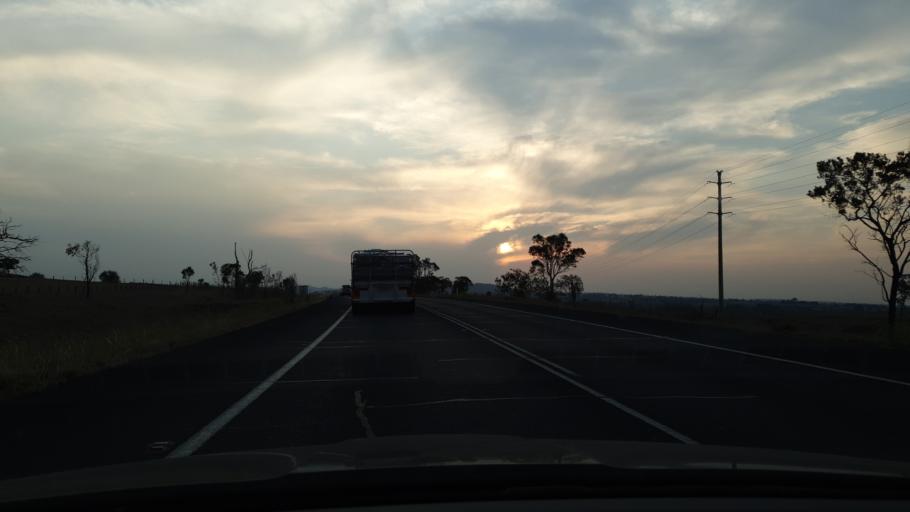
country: AU
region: New South Wales
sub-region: Glen Innes Severn
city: Glen Innes
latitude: -29.6937
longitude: 151.7529
